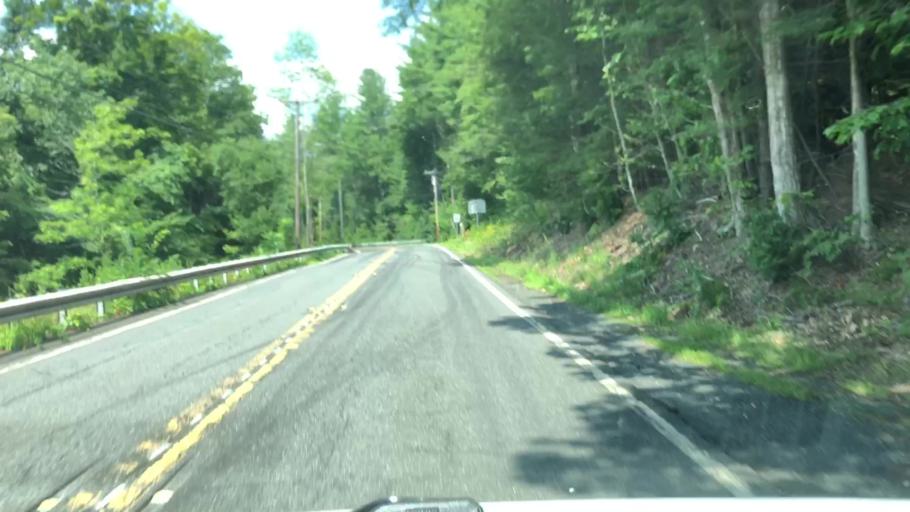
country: US
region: Massachusetts
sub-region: Franklin County
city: Ashfield
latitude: 42.5160
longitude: -72.7458
